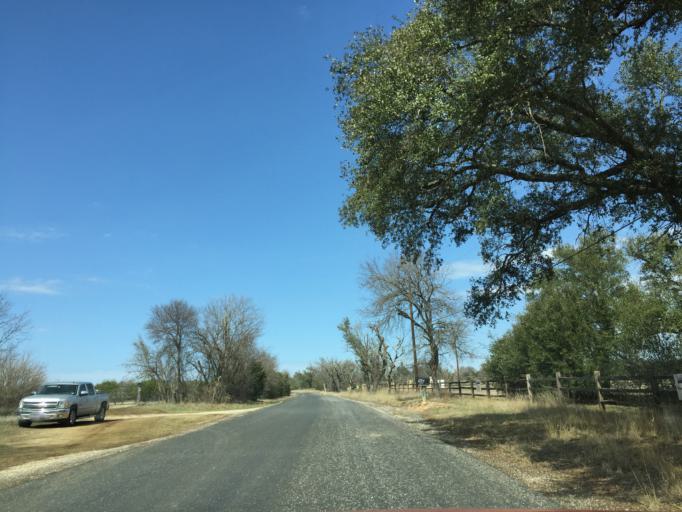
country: US
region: Texas
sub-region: Burnet County
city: Bertram
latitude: 30.7561
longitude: -97.9362
